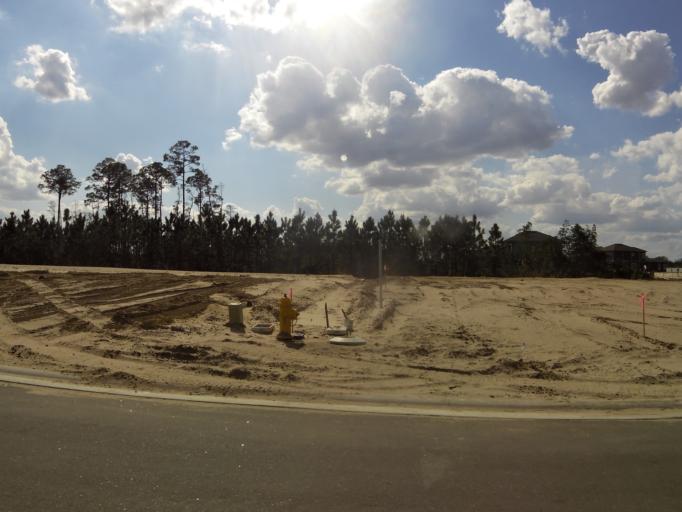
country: US
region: Florida
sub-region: Saint Johns County
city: Palm Valley
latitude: 30.1908
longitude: -81.5013
